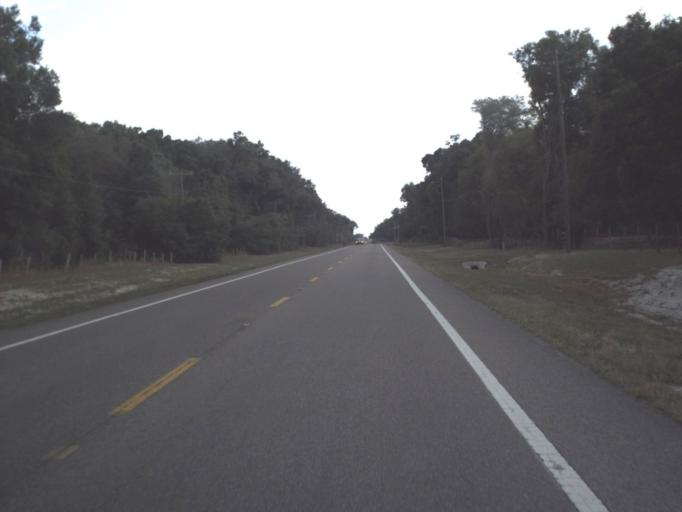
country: US
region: Florida
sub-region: Sumter County
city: Bushnell
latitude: 28.6740
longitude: -82.0548
